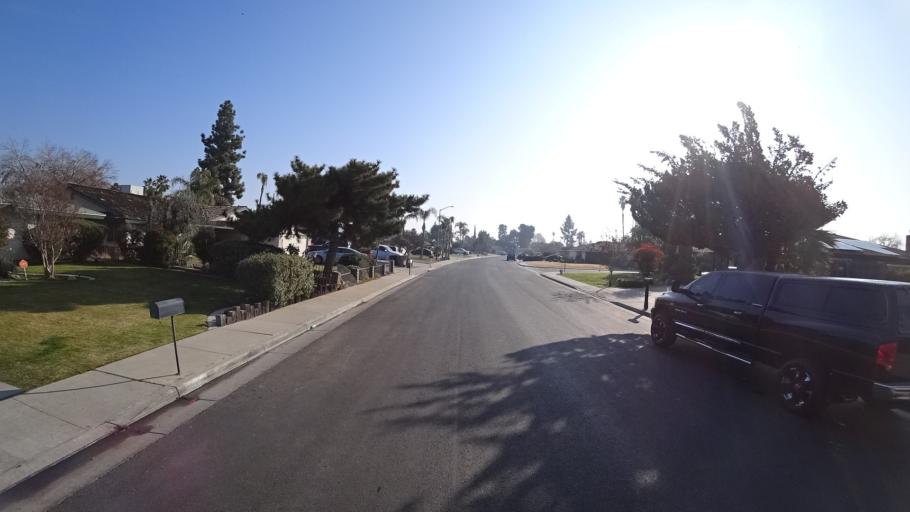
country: US
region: California
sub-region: Kern County
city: Greenacres
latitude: 35.3309
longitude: -119.0725
